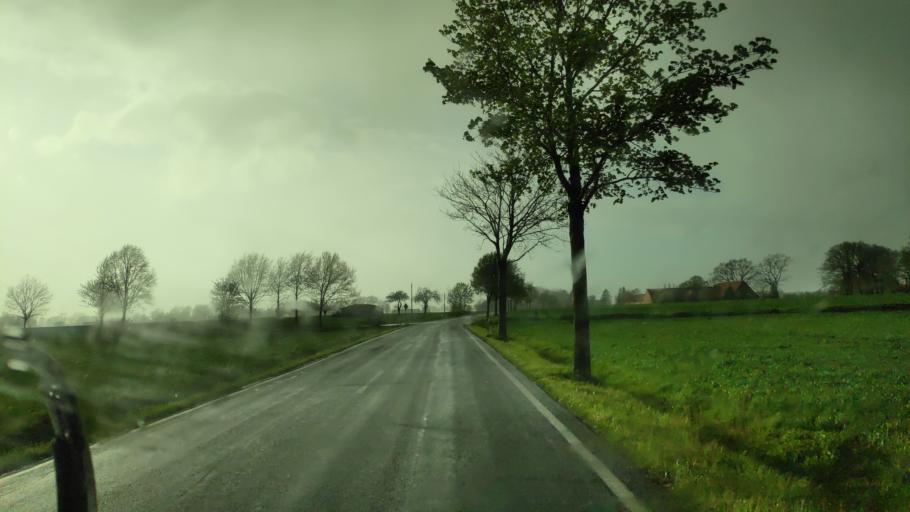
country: DE
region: North Rhine-Westphalia
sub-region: Regierungsbezirk Detmold
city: Hille
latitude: 52.3457
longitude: 8.8250
